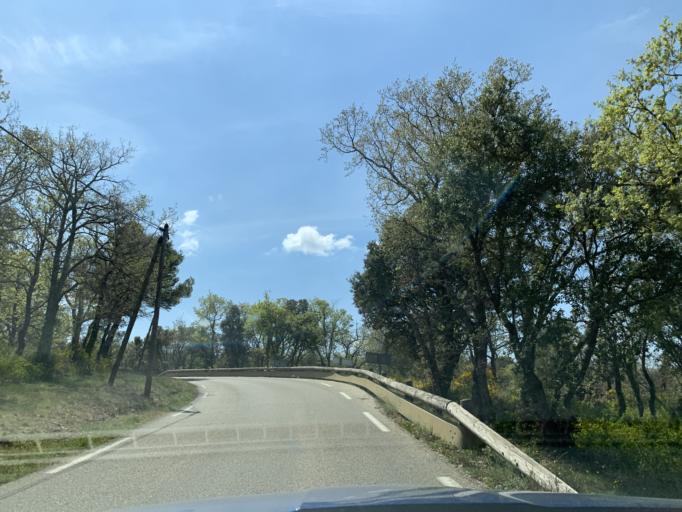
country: FR
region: Provence-Alpes-Cote d'Azur
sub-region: Departement du Vaucluse
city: Saint-Didier
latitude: 43.9719
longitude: 5.1138
